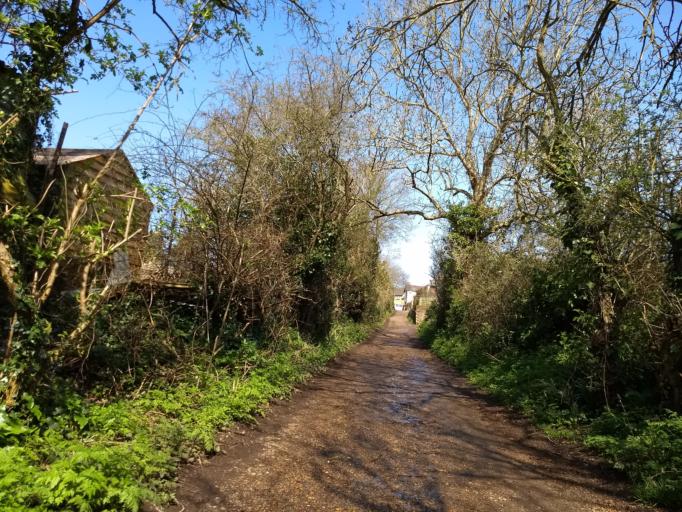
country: GB
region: England
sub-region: Isle of Wight
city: Ryde
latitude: 50.7209
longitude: -1.1633
